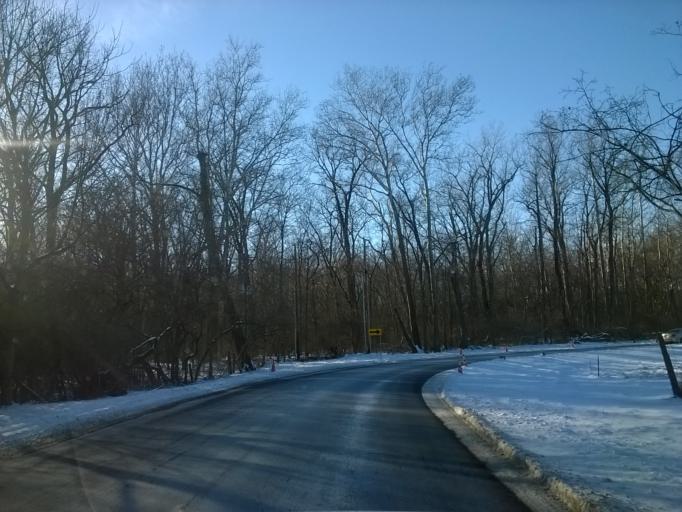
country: US
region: Indiana
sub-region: Boone County
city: Zionsville
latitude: 39.9248
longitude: -86.2780
